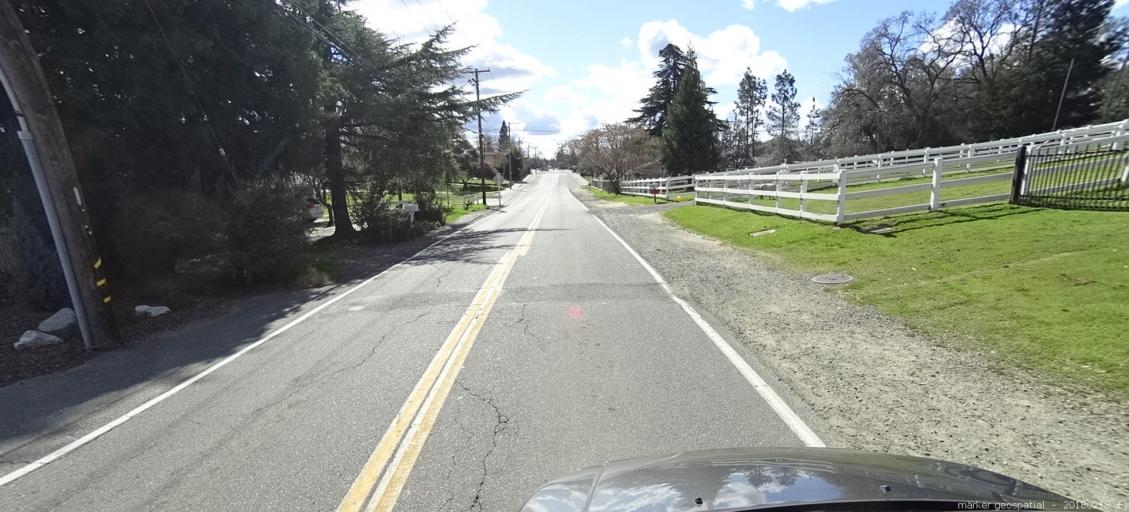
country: US
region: California
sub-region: Sacramento County
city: Orangevale
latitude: 38.6810
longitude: -121.2115
